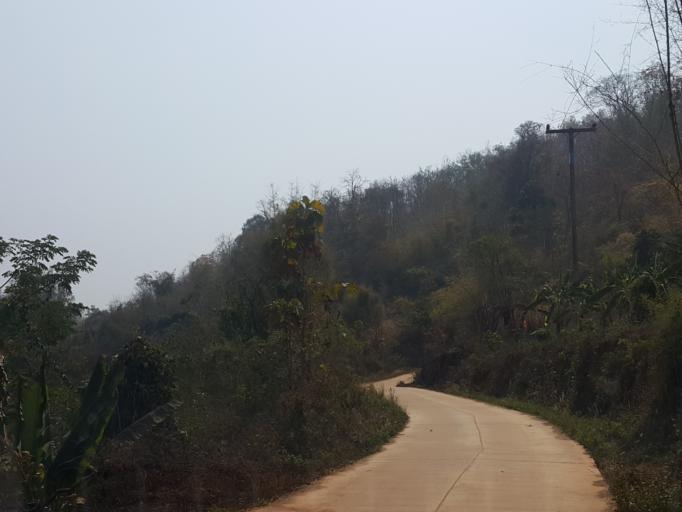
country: TH
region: Chiang Mai
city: Hang Dong
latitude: 18.7478
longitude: 98.8259
